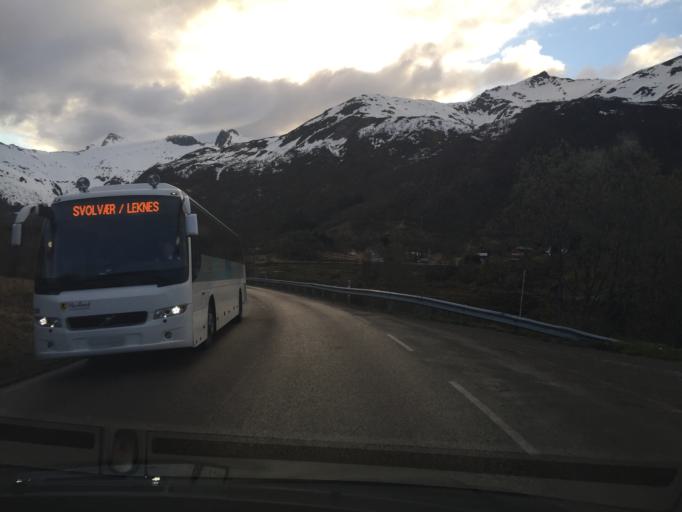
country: NO
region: Nordland
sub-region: Vagan
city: Svolvaer
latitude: 68.3240
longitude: 14.6982
